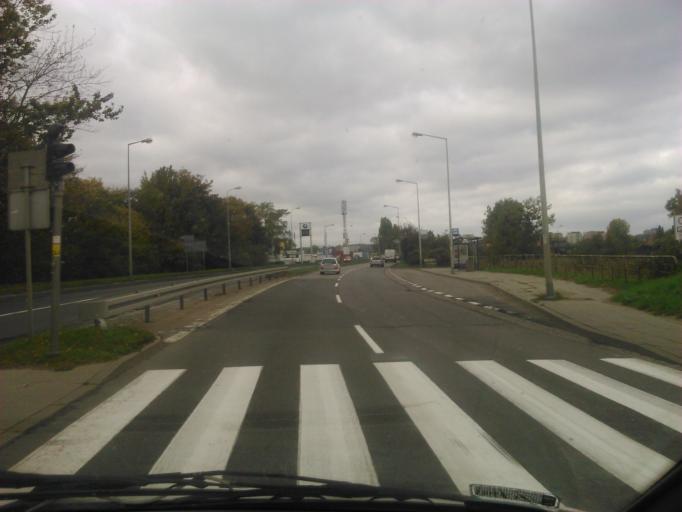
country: PL
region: Pomeranian Voivodeship
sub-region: Gdansk
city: Gdansk
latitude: 54.3490
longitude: 18.6917
